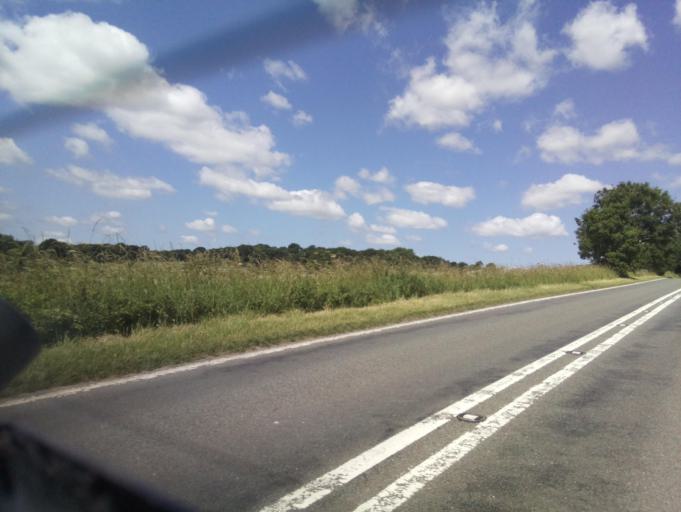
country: GB
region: England
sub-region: Derbyshire
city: Bakewell
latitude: 53.1333
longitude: -1.7543
